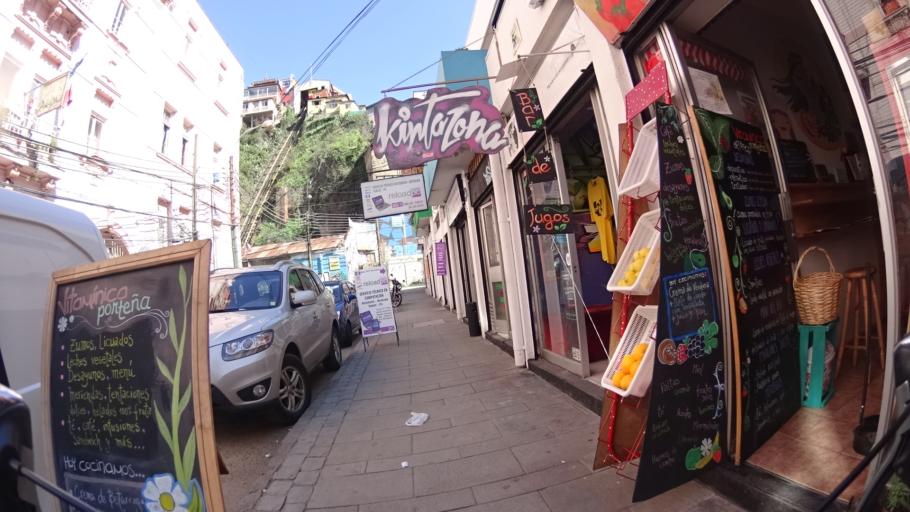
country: CL
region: Valparaiso
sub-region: Provincia de Valparaiso
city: Valparaiso
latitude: -33.0470
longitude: -71.6212
